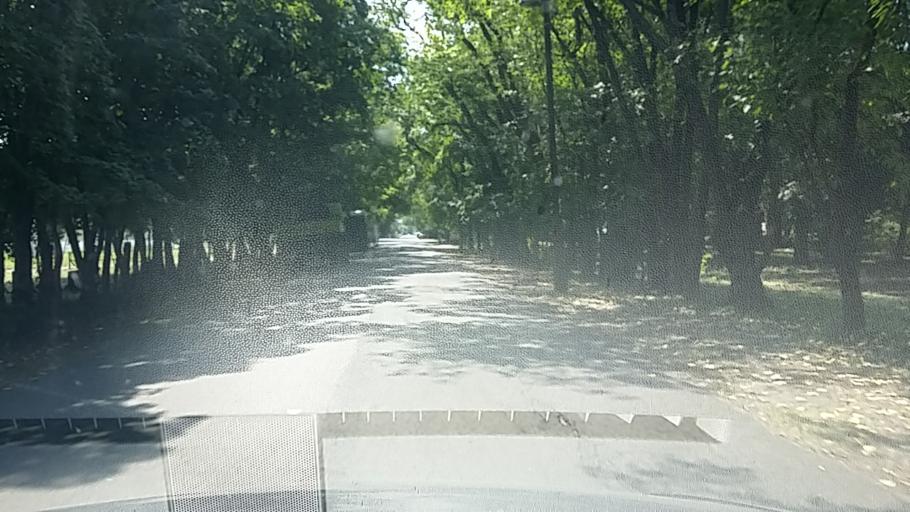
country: HU
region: Bekes
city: Gyomaendrod
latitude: 46.9400
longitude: 20.8381
